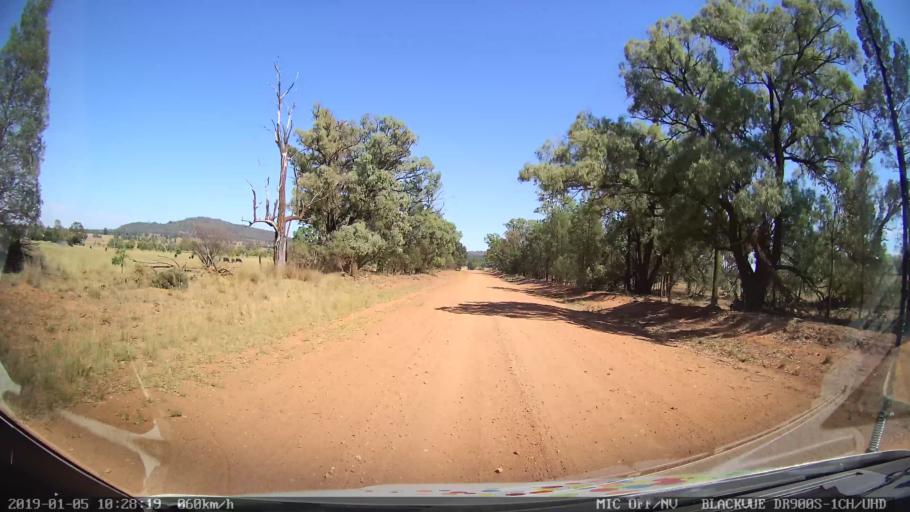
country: AU
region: New South Wales
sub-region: Gilgandra
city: Gilgandra
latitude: -31.5459
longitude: 148.9395
